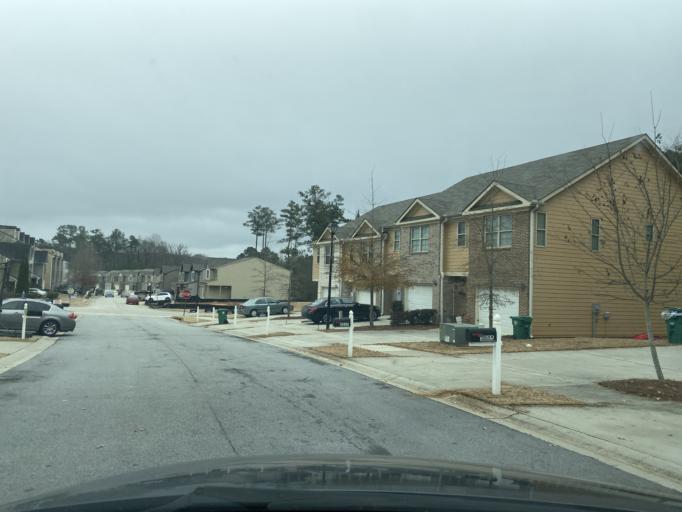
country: US
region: Georgia
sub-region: DeKalb County
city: Pine Mountain
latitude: 33.6891
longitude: -84.1556
